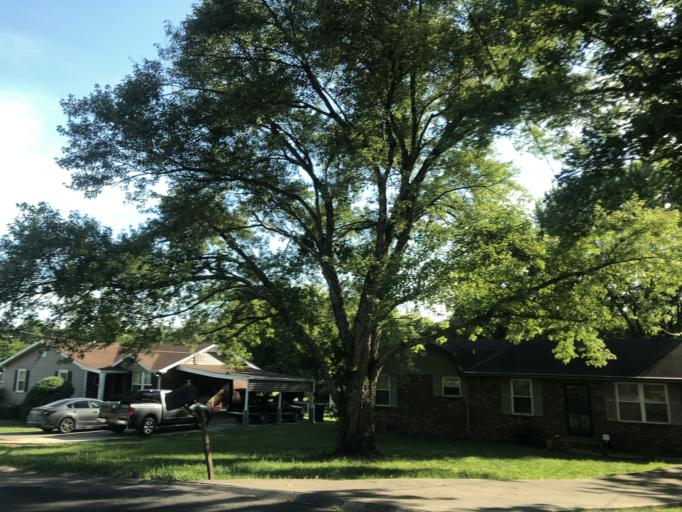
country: US
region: Tennessee
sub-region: Davidson County
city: Nashville
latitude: 36.2237
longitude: -86.8503
